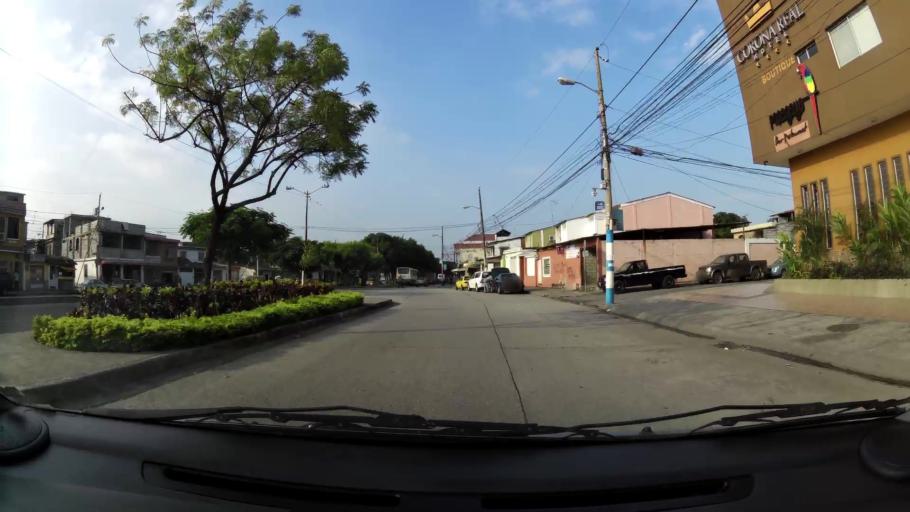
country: EC
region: Guayas
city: Eloy Alfaro
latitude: -2.1299
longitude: -79.8968
